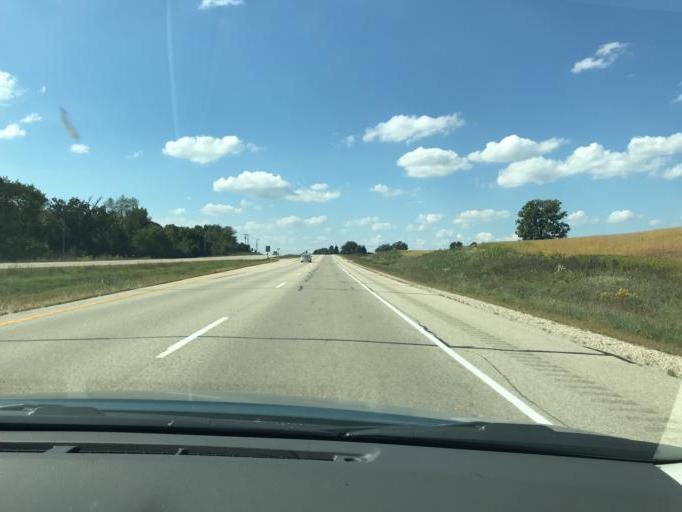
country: US
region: Wisconsin
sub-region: Walworth County
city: Pell Lake
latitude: 42.5920
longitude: -88.3454
